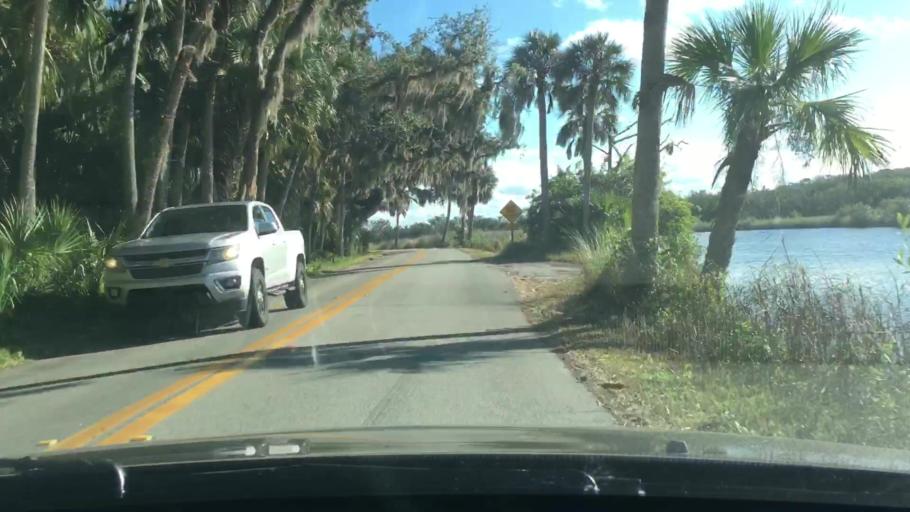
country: US
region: Florida
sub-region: Flagler County
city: Flagler Beach
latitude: 29.4079
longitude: -81.1184
